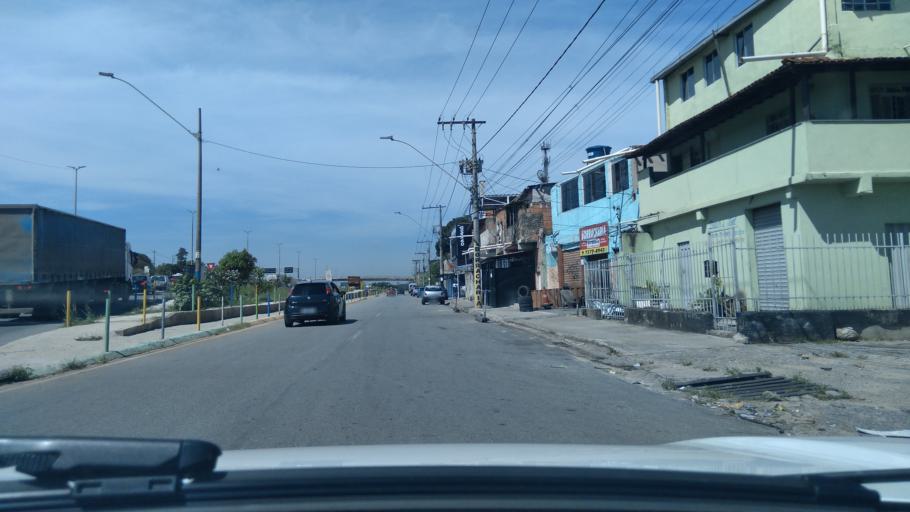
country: BR
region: Minas Gerais
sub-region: Belo Horizonte
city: Belo Horizonte
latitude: -19.9061
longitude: -43.9899
